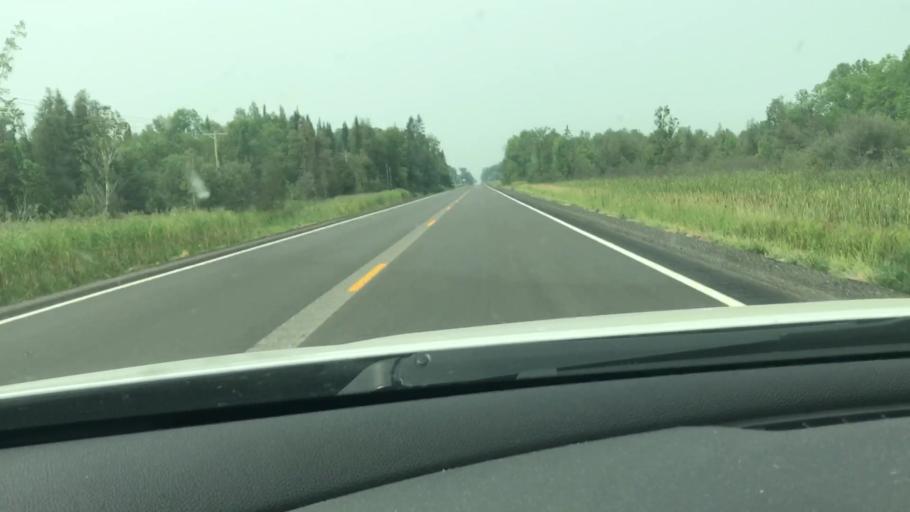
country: US
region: Minnesota
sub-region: Itasca County
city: Cohasset
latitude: 47.3526
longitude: -93.8432
